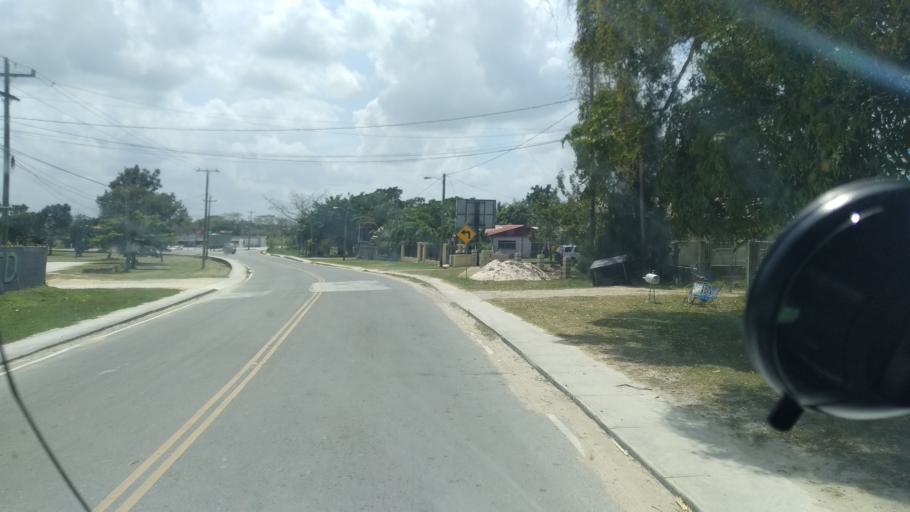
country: BZ
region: Orange Walk
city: Orange Walk
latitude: 18.0639
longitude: -88.5721
